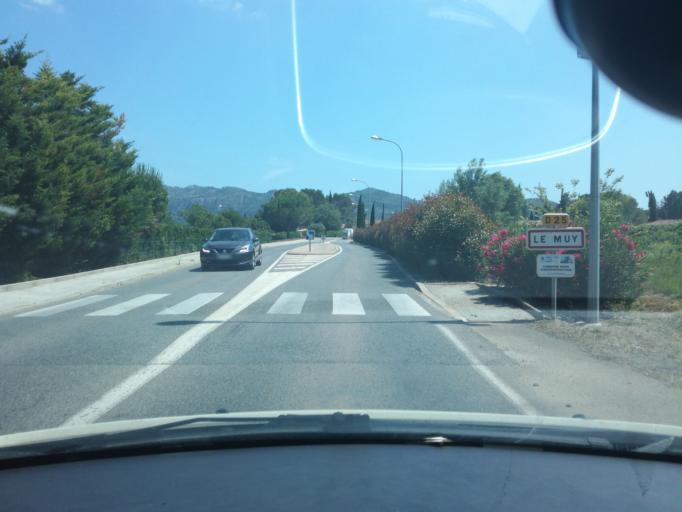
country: FR
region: Provence-Alpes-Cote d'Azur
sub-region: Departement du Var
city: Le Muy
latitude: 43.4796
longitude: 6.5657
